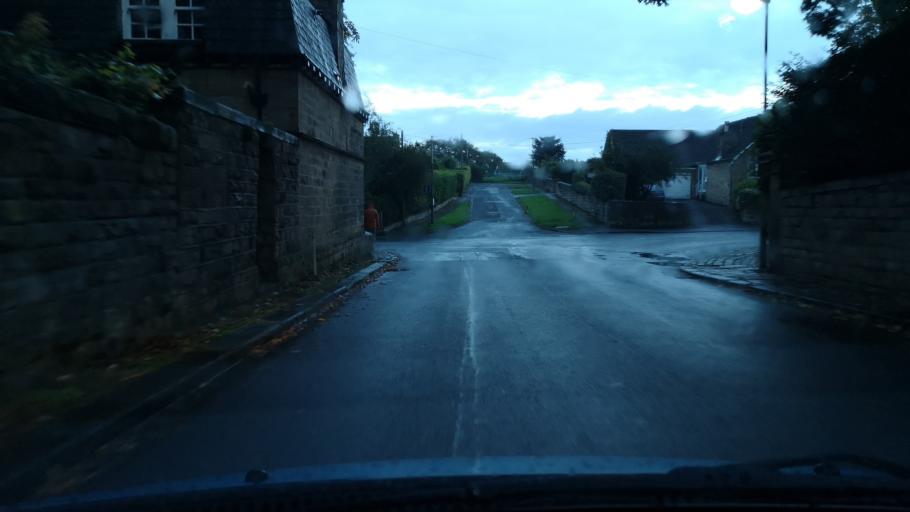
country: GB
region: England
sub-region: Kirklees
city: Batley
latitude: 53.7237
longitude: -1.6349
